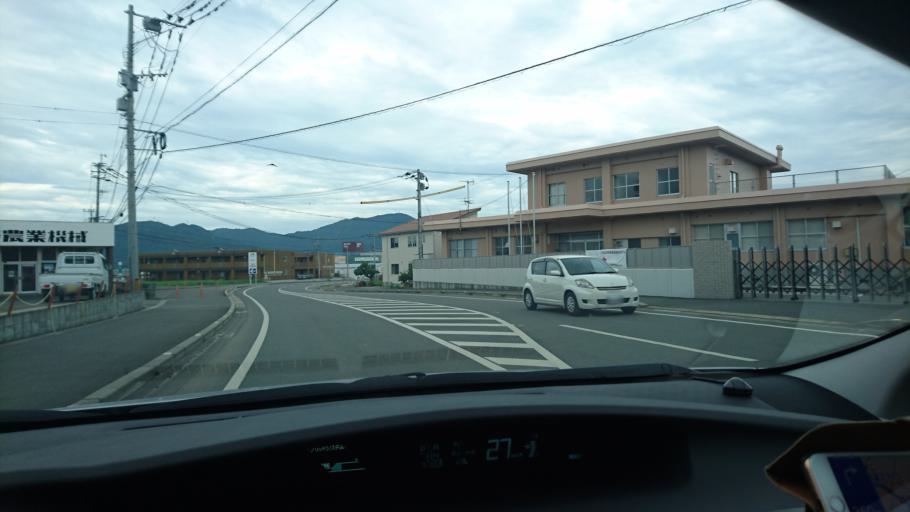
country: JP
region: Saga Prefecture
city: Takeocho-takeo
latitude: 33.2015
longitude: 130.0317
